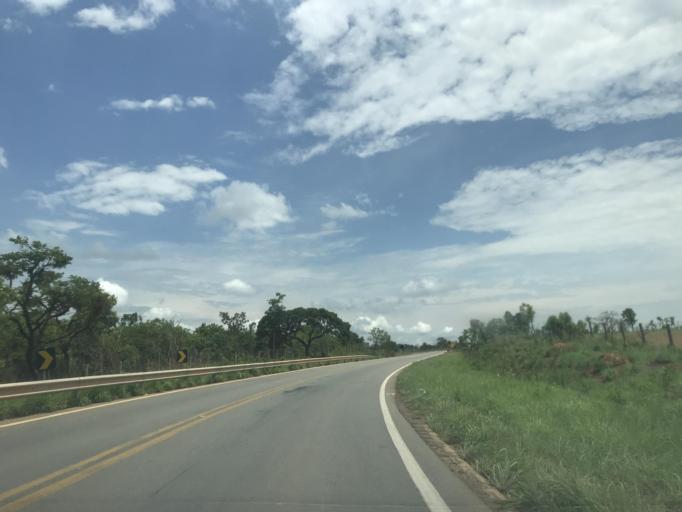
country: BR
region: Goias
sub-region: Luziania
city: Luziania
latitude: -16.3933
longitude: -48.1402
